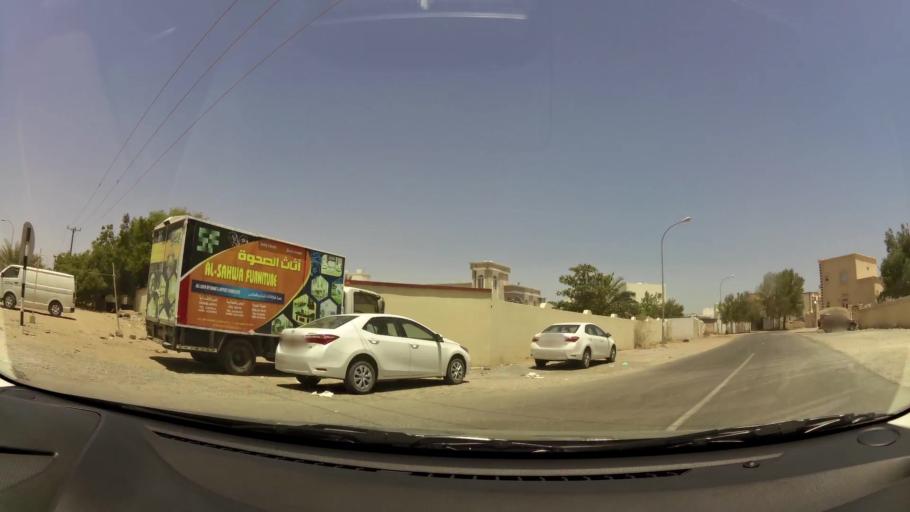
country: OM
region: Muhafazat Masqat
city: As Sib al Jadidah
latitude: 23.6283
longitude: 58.2410
